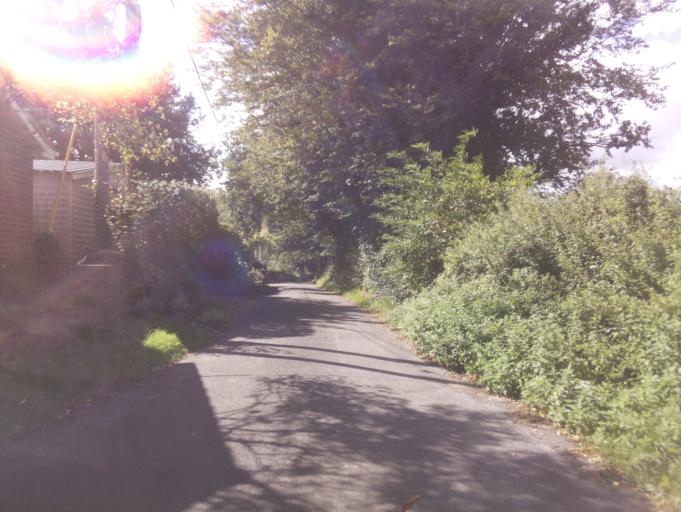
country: GB
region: England
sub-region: Wiltshire
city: Erlestoke
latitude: 51.2855
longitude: -2.0684
